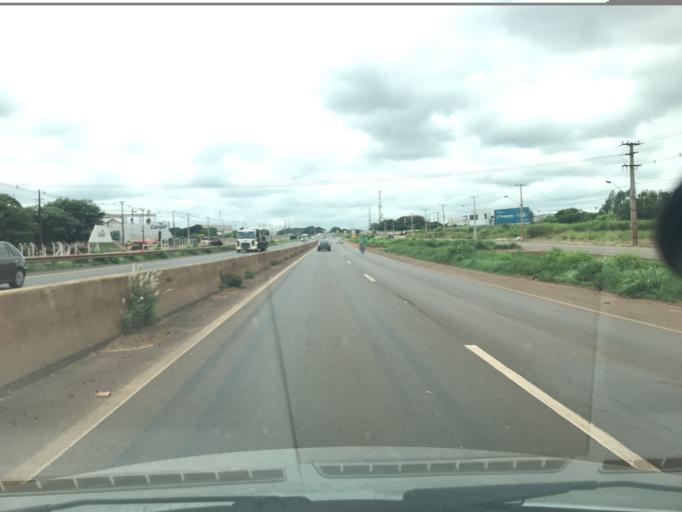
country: BR
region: Parana
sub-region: Paicandu
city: Paicandu
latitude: -23.4462
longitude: -51.9945
